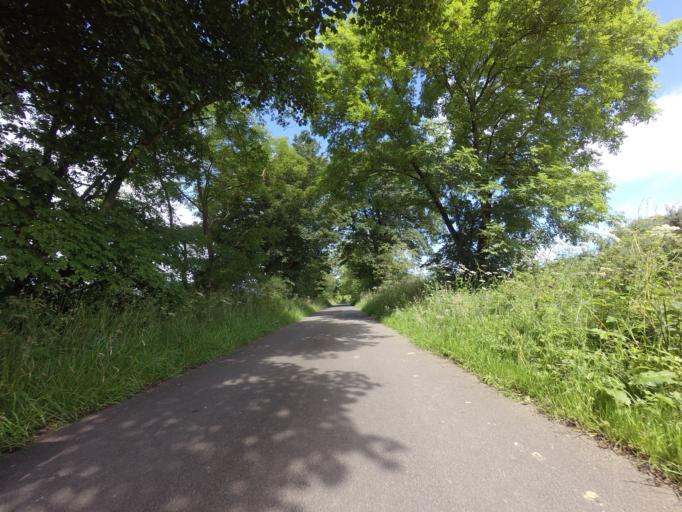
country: GB
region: Scotland
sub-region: Aberdeenshire
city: Turriff
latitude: 57.5899
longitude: -2.5050
